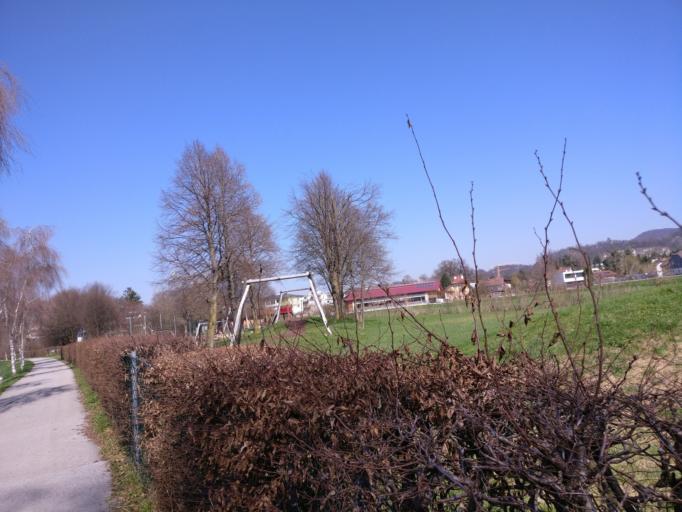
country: AT
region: Salzburg
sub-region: Salzburg Stadt
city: Salzburg
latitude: 47.7891
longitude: 13.0211
